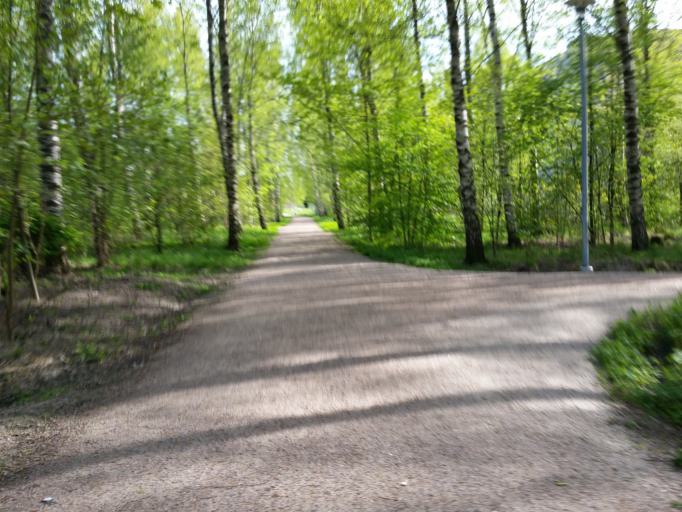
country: FI
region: Uusimaa
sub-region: Helsinki
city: Koukkuniemi
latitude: 60.1766
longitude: 24.7653
